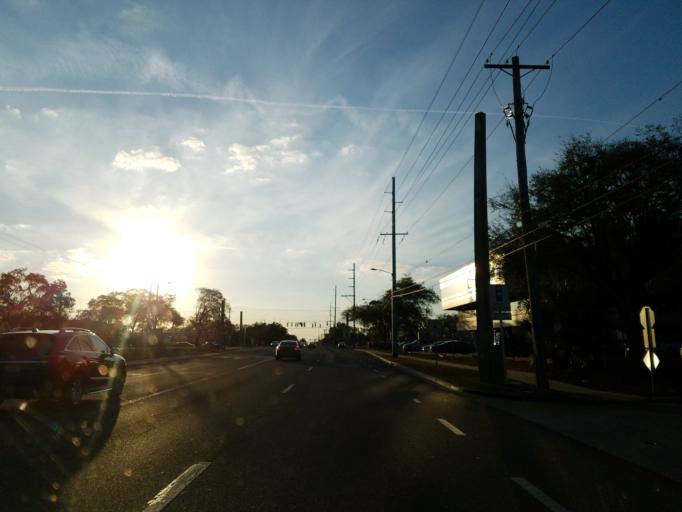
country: US
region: Florida
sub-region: Hillsborough County
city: University
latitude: 28.0693
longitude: -82.4243
